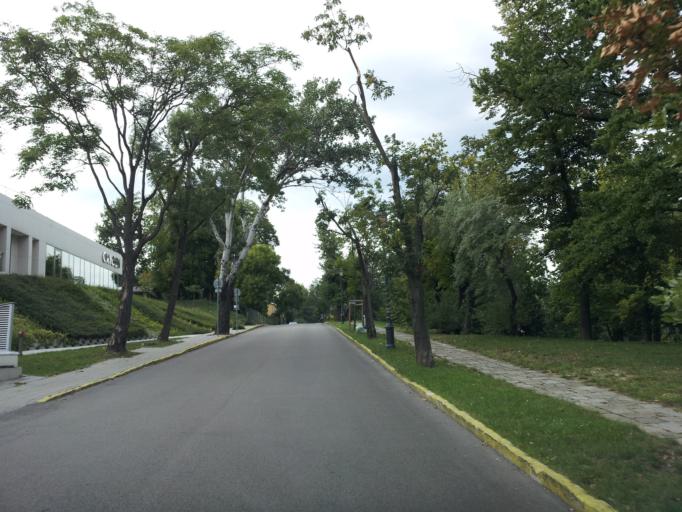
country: HU
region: Budapest
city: Budapest I. keruelet
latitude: 47.4910
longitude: 19.0383
